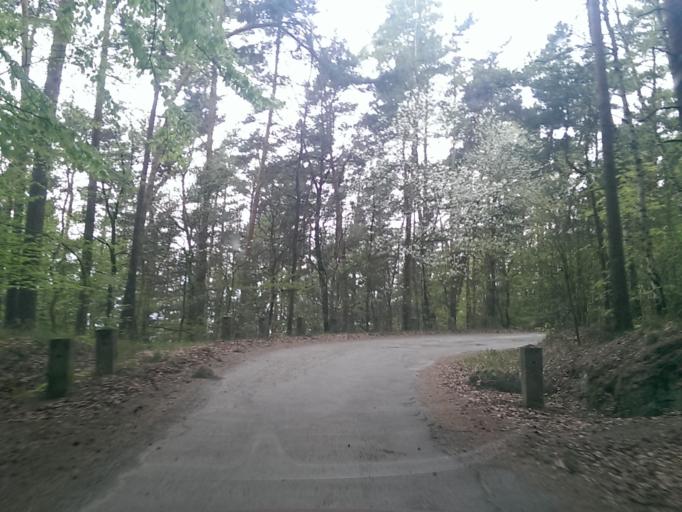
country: CZ
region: Central Bohemia
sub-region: Okres Mlada Boleslav
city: Zd'ar
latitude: 50.5509
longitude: 15.1229
